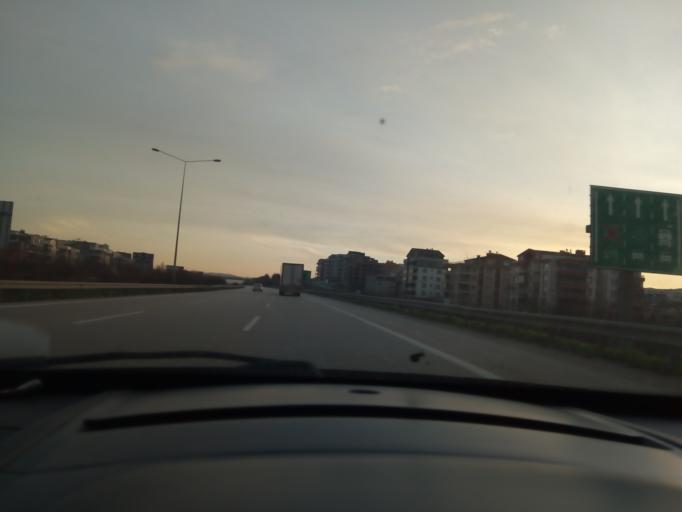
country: TR
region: Bursa
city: Niluefer
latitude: 40.2660
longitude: 28.9531
